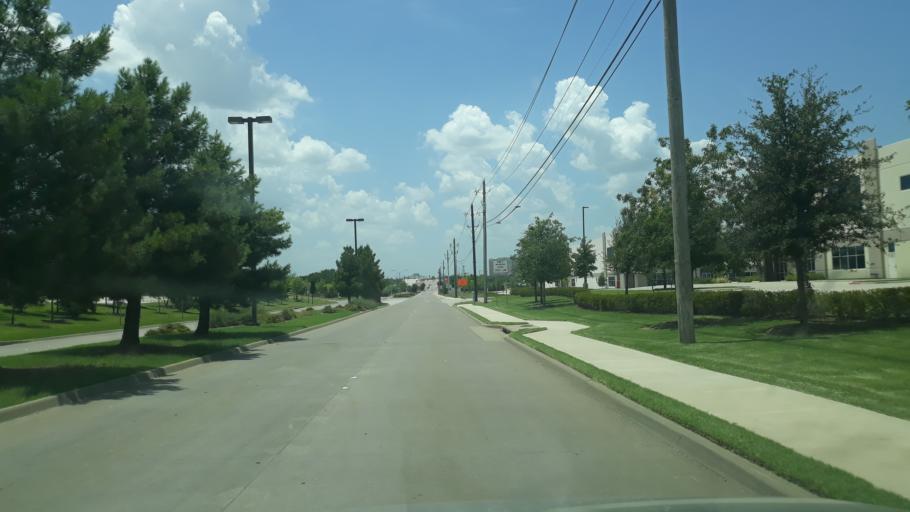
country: US
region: Texas
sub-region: Dallas County
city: Coppell
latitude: 32.9551
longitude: -97.0306
